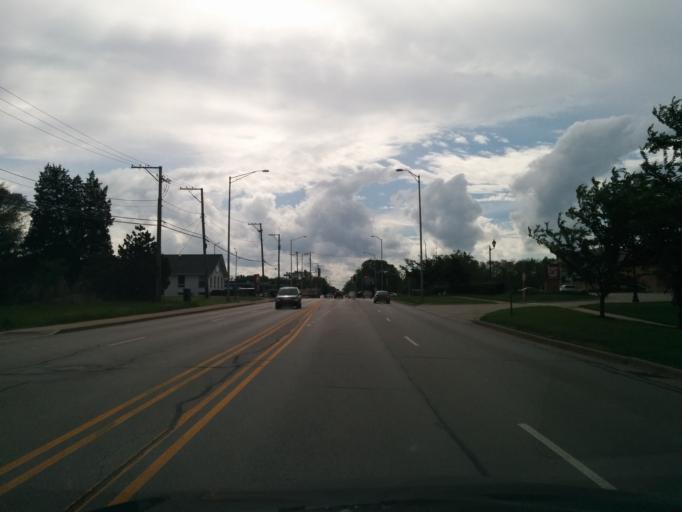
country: US
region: Illinois
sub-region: Will County
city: Romeoville
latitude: 41.6401
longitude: -88.0783
